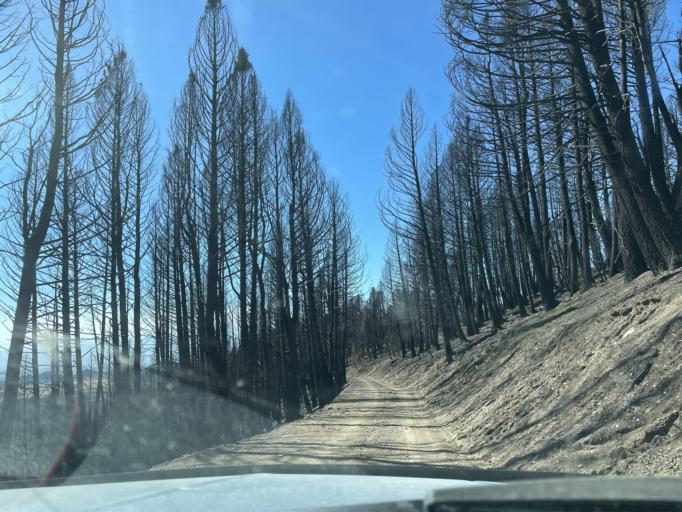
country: US
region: Montana
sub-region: Broadwater County
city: Townsend
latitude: 46.5073
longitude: -111.2792
